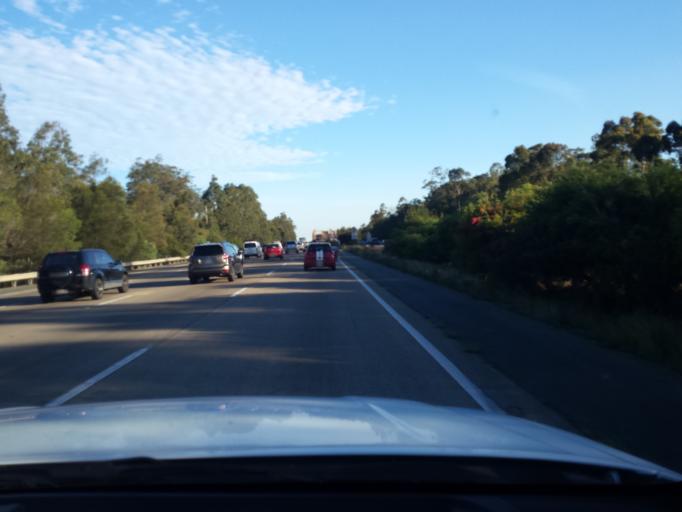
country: AU
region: Queensland
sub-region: Gold Coast
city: Oxenford
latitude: -27.8370
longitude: 153.3029
